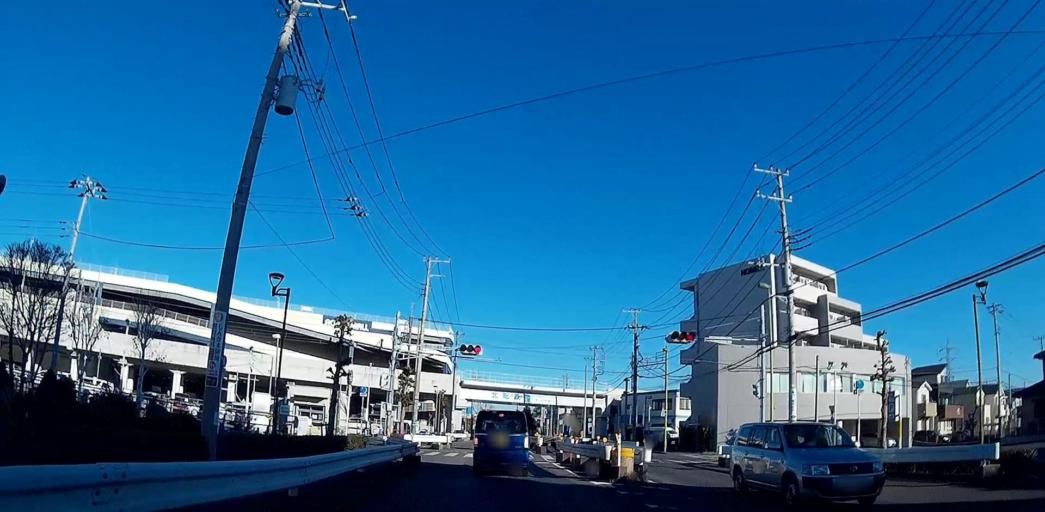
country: JP
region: Chiba
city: Shiroi
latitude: 35.7799
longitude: 140.0021
